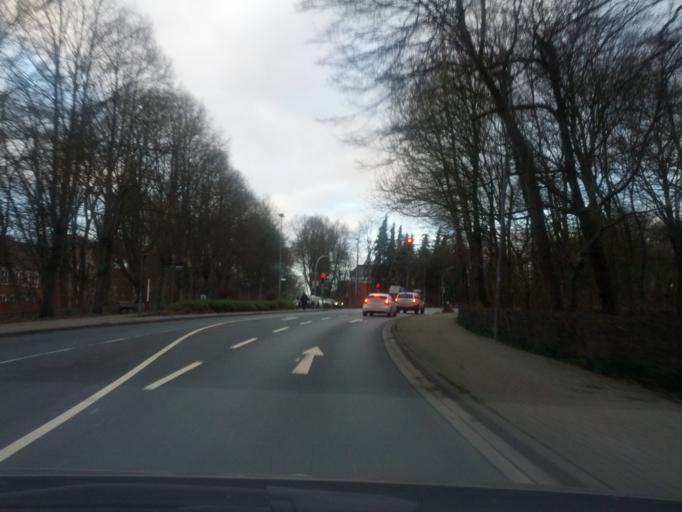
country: DE
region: Lower Saxony
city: Rotenburg
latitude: 53.1105
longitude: 9.3940
